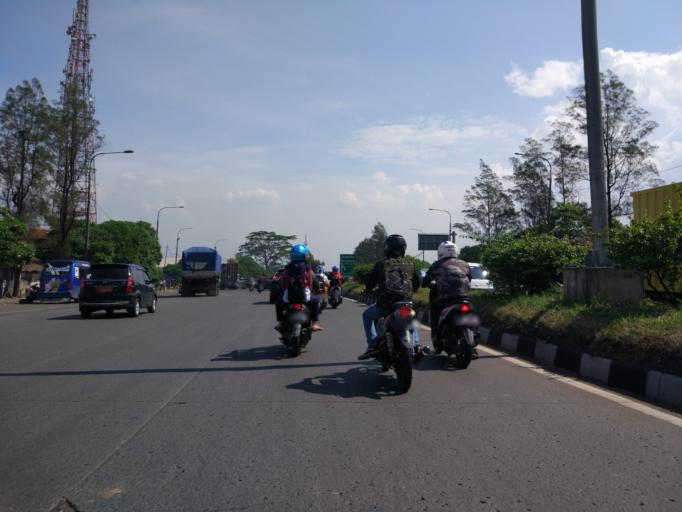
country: ID
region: West Java
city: Cileunyi
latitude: -6.9423
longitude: 107.7543
